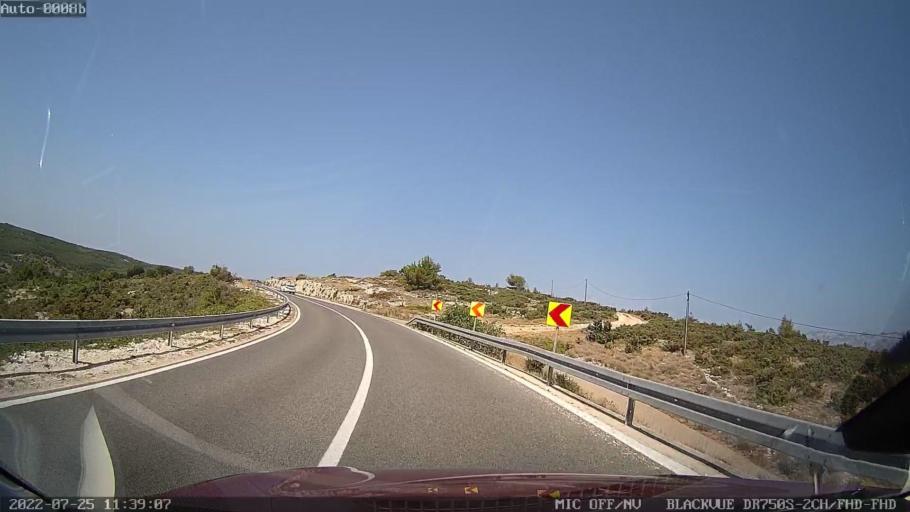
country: HR
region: Zadarska
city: Razanac
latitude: 44.2563
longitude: 15.3752
